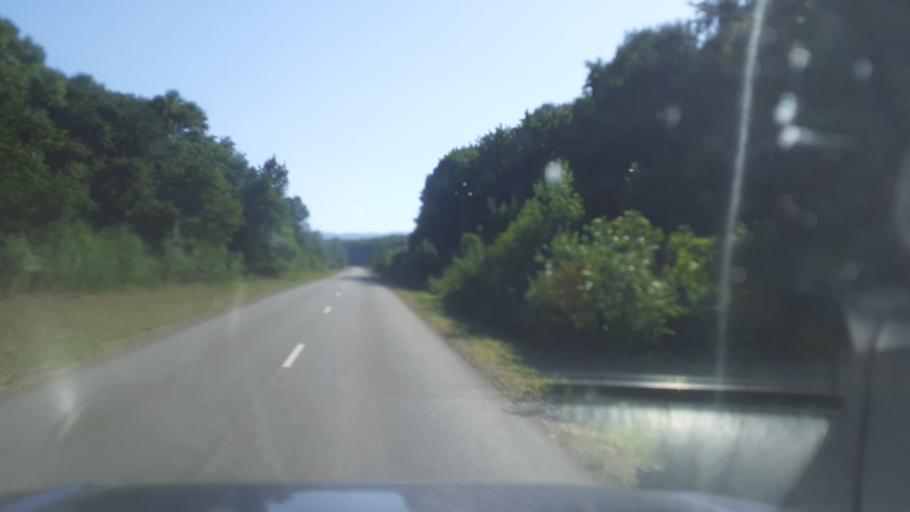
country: RU
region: Krasnodarskiy
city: Azovskaya
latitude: 44.7614
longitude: 38.5642
